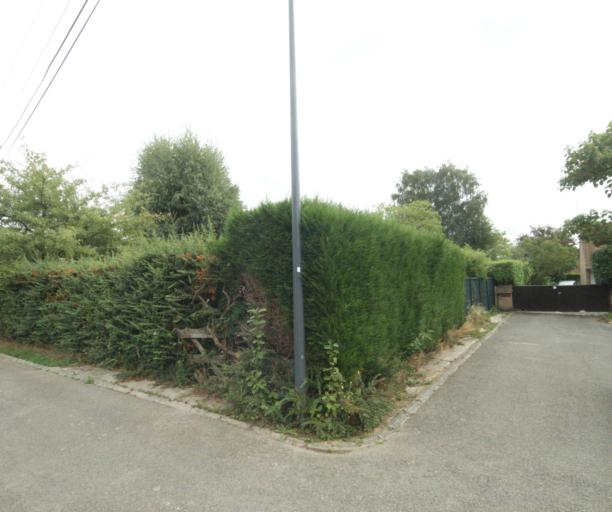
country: FR
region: Nord-Pas-de-Calais
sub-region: Departement du Nord
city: Villeneuve-d'Ascq
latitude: 50.6179
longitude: 3.1500
